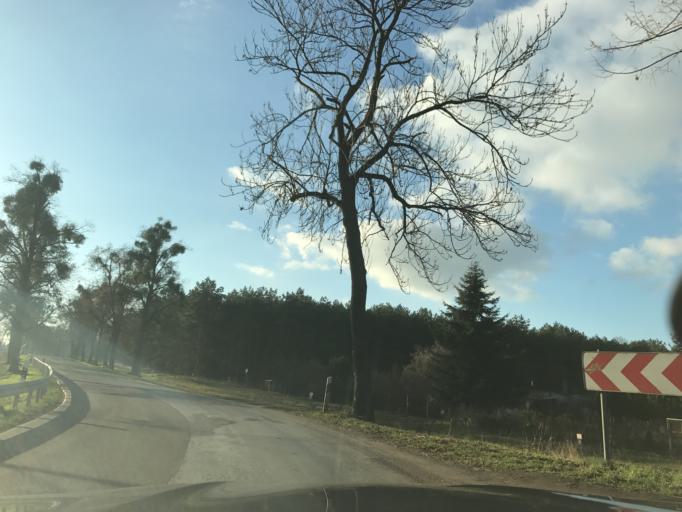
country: DE
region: Saxony-Anhalt
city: Mockern
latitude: 52.1545
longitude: 11.9695
